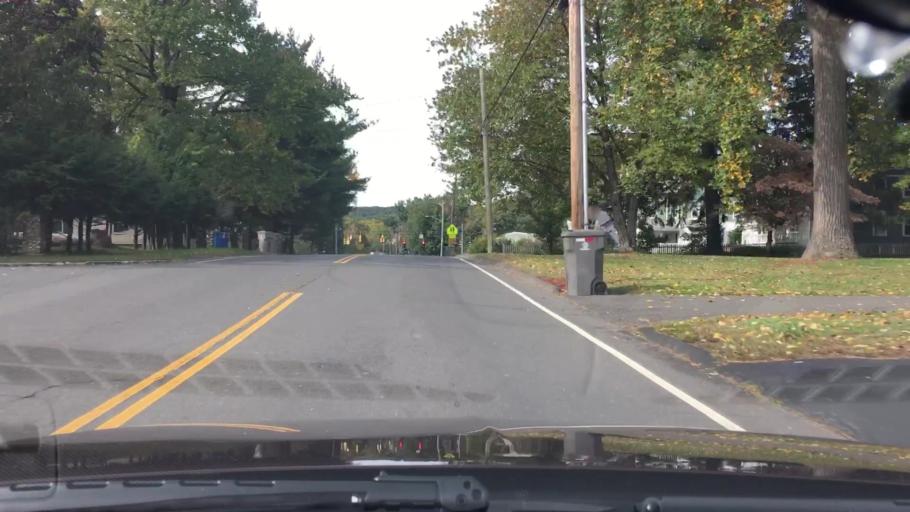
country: US
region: Connecticut
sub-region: Hartford County
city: Plainville
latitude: 41.6773
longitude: -72.9011
